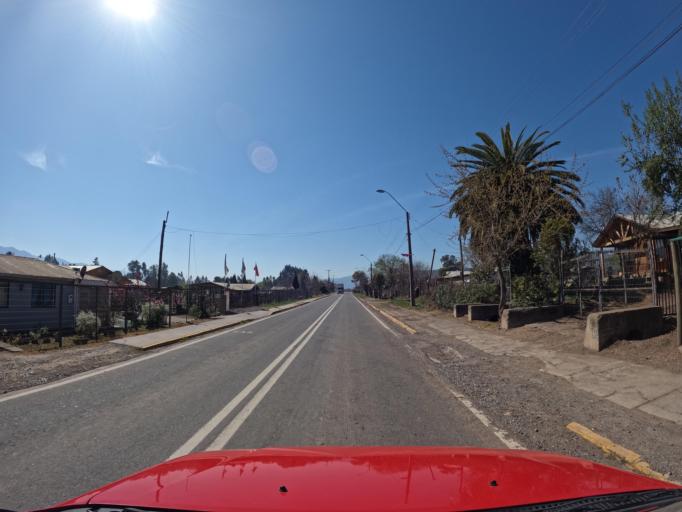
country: CL
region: Maule
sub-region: Provincia de Curico
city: Molina
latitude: -35.0557
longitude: -71.4861
